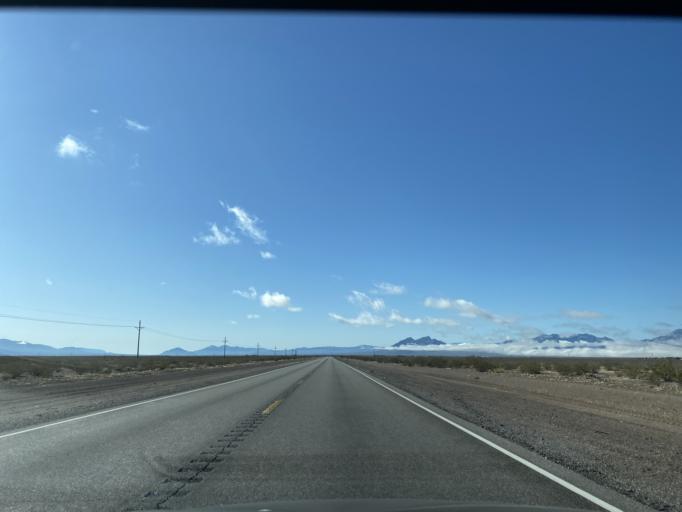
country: US
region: Nevada
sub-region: Nye County
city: Beatty
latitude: 36.5611
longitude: -116.4150
